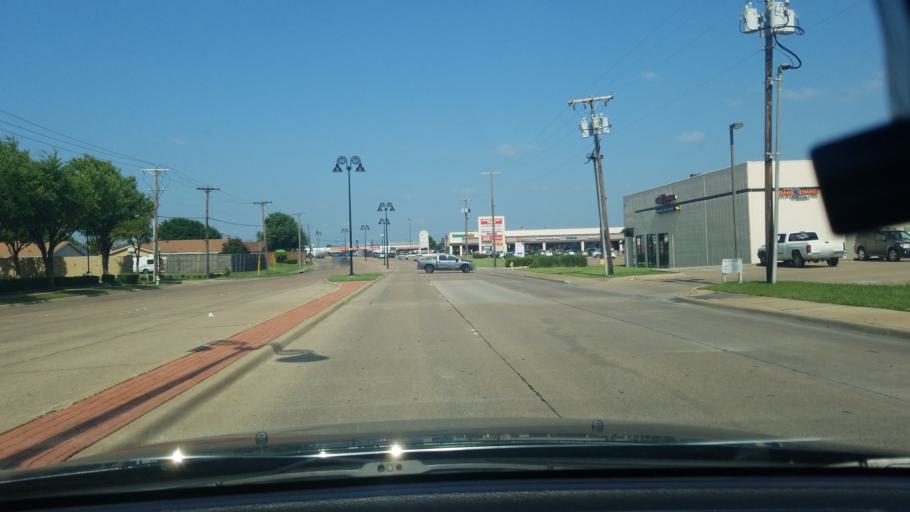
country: US
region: Texas
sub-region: Dallas County
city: Mesquite
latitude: 32.8107
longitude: -96.6144
